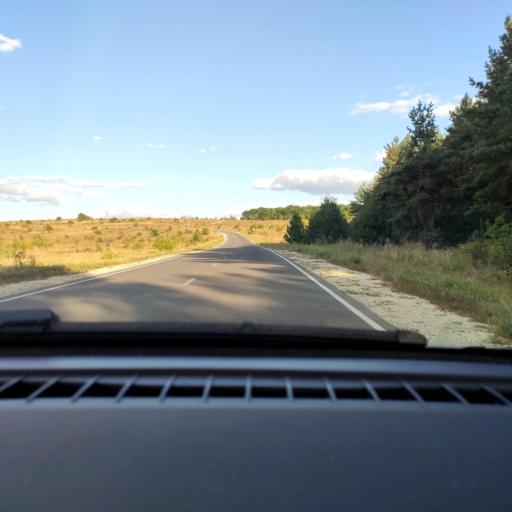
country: RU
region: Voronezj
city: Semiluki
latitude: 51.6572
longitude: 38.9953
